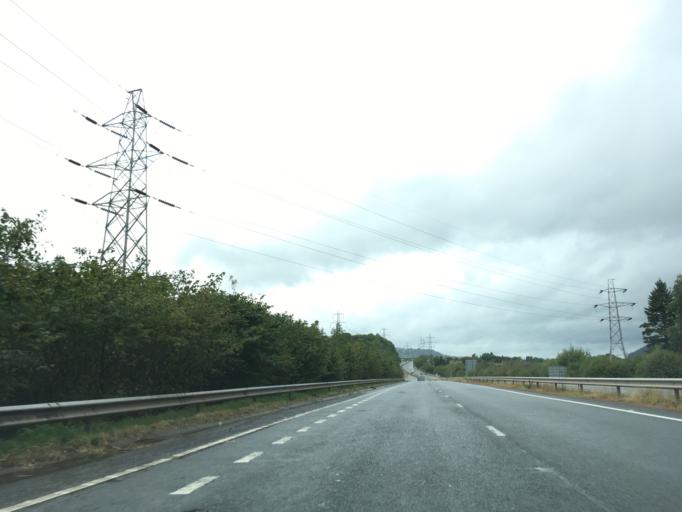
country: GB
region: Wales
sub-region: Monmouthshire
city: Abergavenny
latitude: 51.8167
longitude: -3.0331
